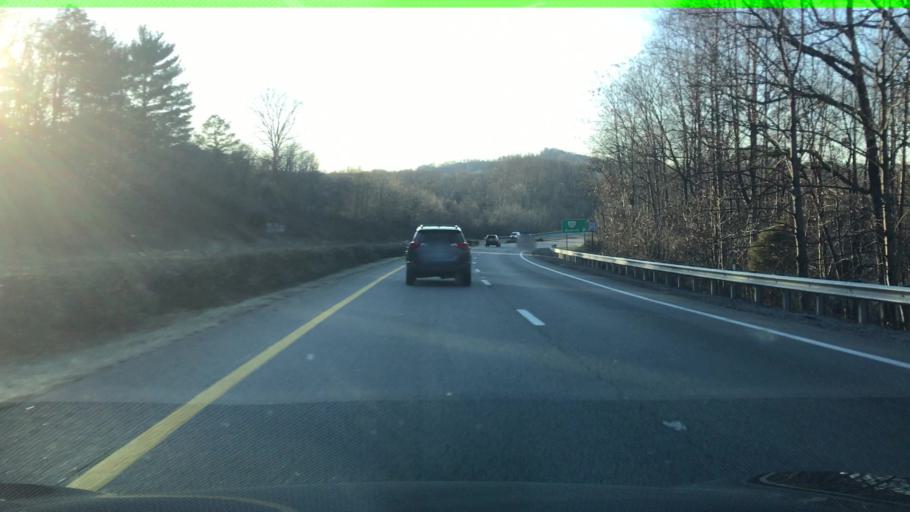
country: US
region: Virginia
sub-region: City of Bedford
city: Bedford
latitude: 37.3228
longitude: -79.5258
